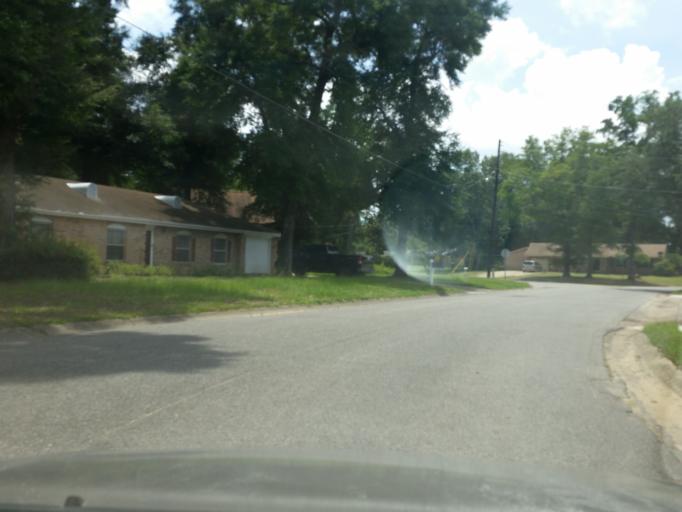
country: US
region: Florida
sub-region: Escambia County
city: Ferry Pass
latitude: 30.5128
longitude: -87.1941
